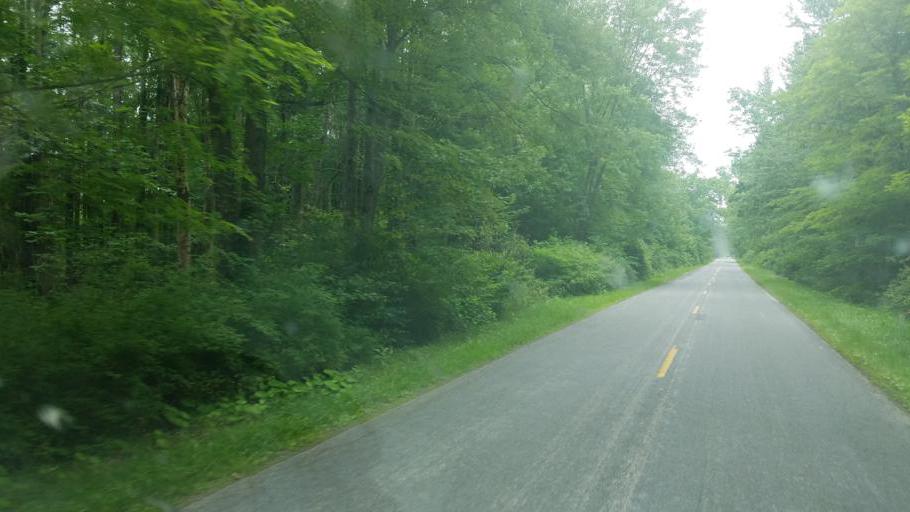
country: US
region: Ohio
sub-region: Trumbull County
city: Cortland
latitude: 41.4338
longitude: -80.7773
